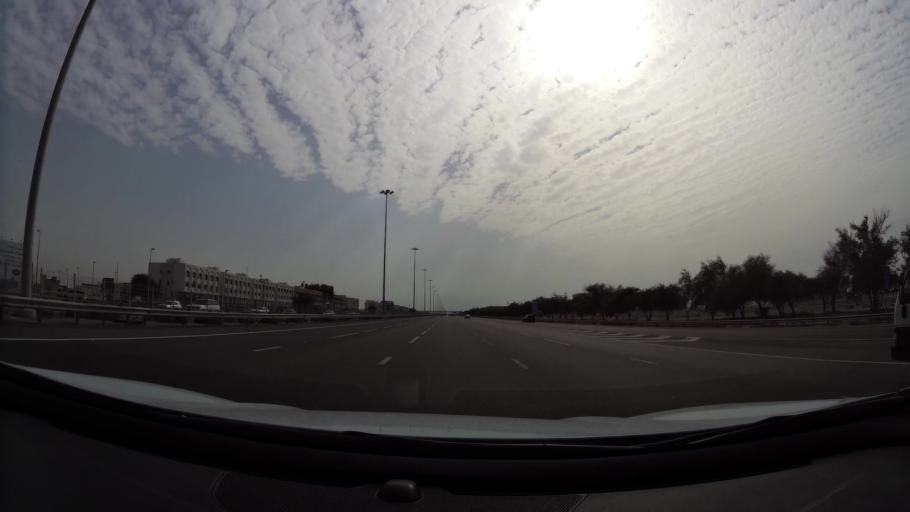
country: AE
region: Abu Dhabi
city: Abu Dhabi
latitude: 24.5357
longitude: 54.6828
